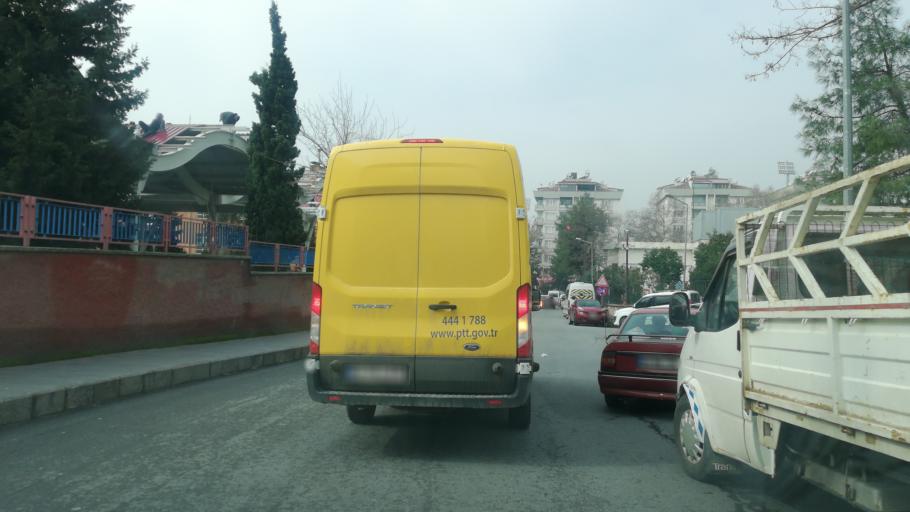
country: TR
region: Kahramanmaras
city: Kahramanmaras
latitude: 37.5735
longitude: 36.9273
